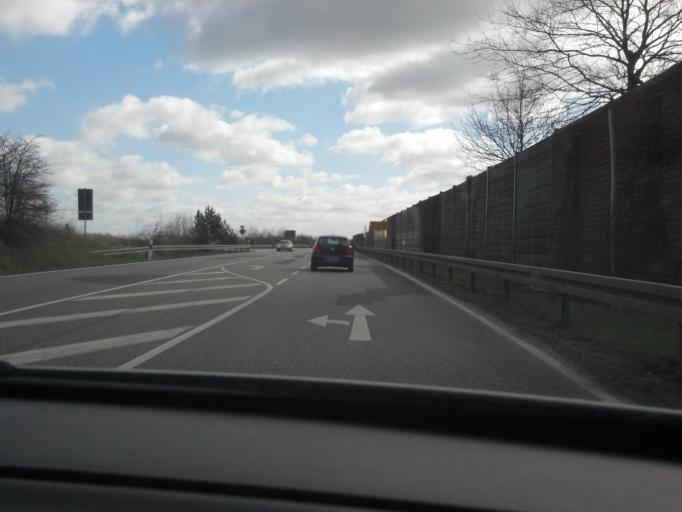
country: DE
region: Mecklenburg-Vorpommern
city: Boizenburg
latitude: 53.3892
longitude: 10.7304
